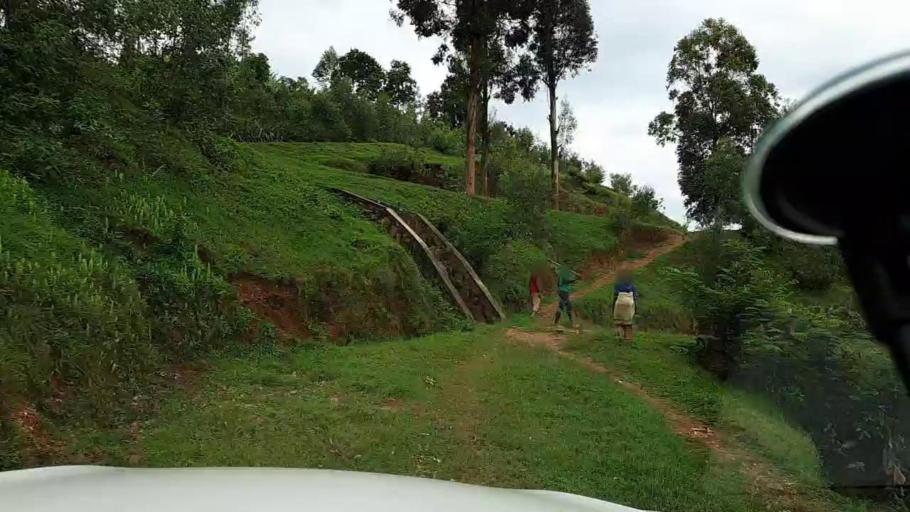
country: RW
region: Southern Province
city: Gitarama
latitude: -2.0842
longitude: 29.6478
